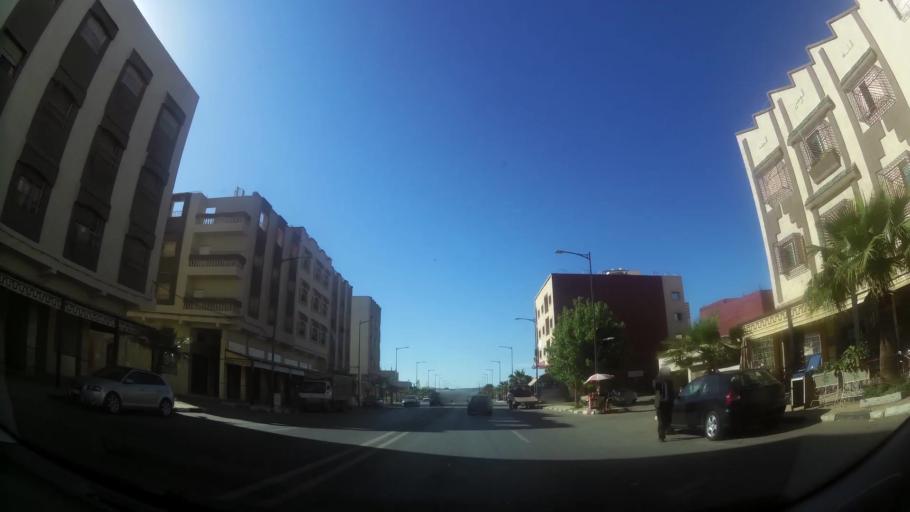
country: MA
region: Oriental
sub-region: Berkane-Taourirt
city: Ahfir
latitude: 34.8620
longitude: -1.9957
